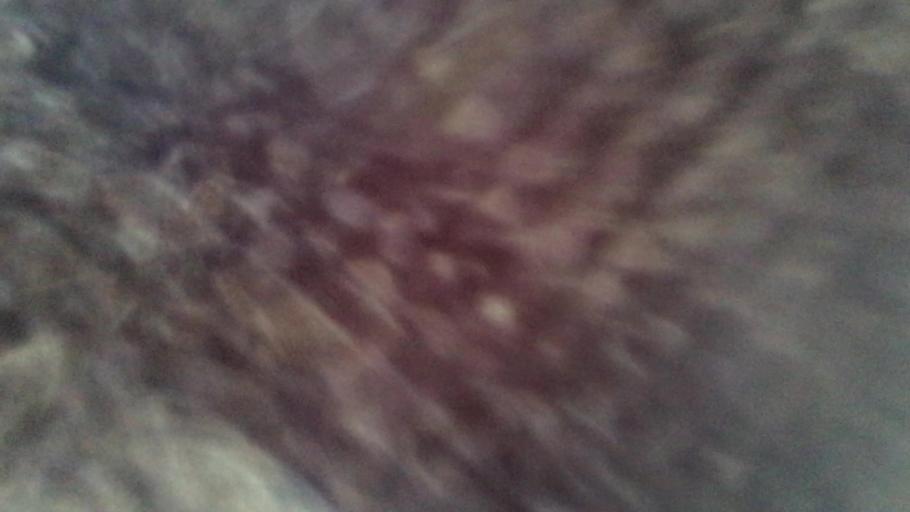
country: US
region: New Jersey
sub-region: Hudson County
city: Guttenberg
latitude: 40.7931
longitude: -73.9914
